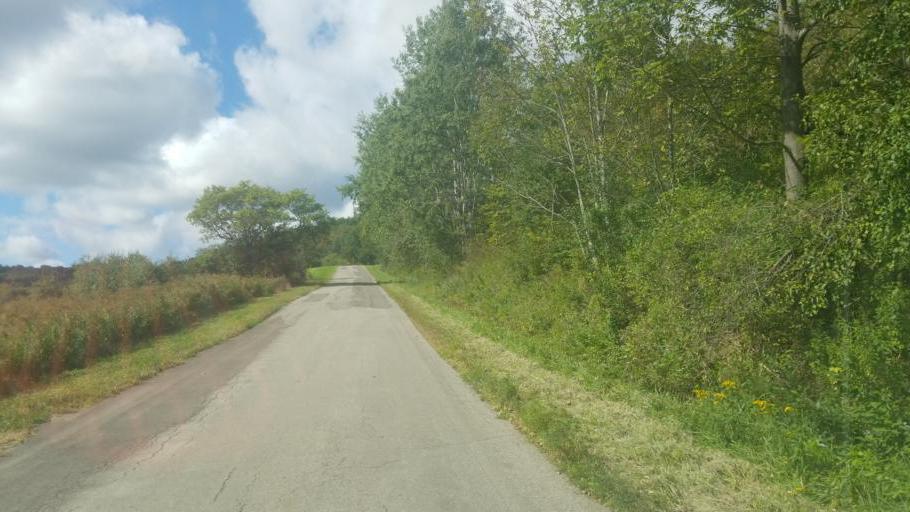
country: US
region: New York
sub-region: Cattaraugus County
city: Franklinville
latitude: 42.2335
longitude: -78.4043
